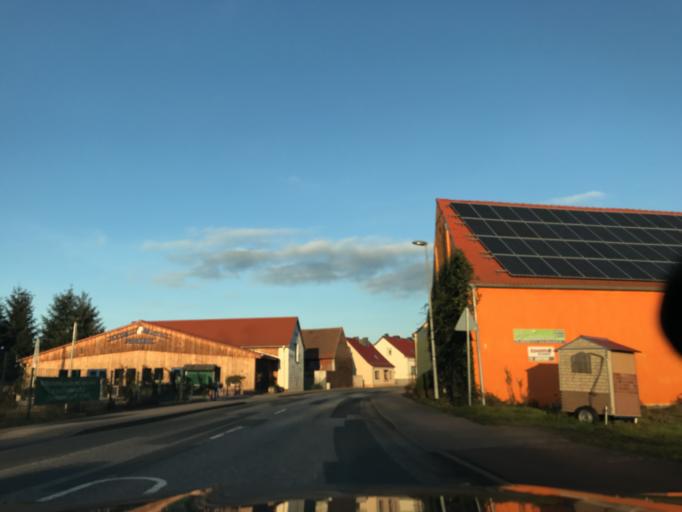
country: DE
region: Saxony-Anhalt
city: Genthin
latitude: 52.3498
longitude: 12.0745
